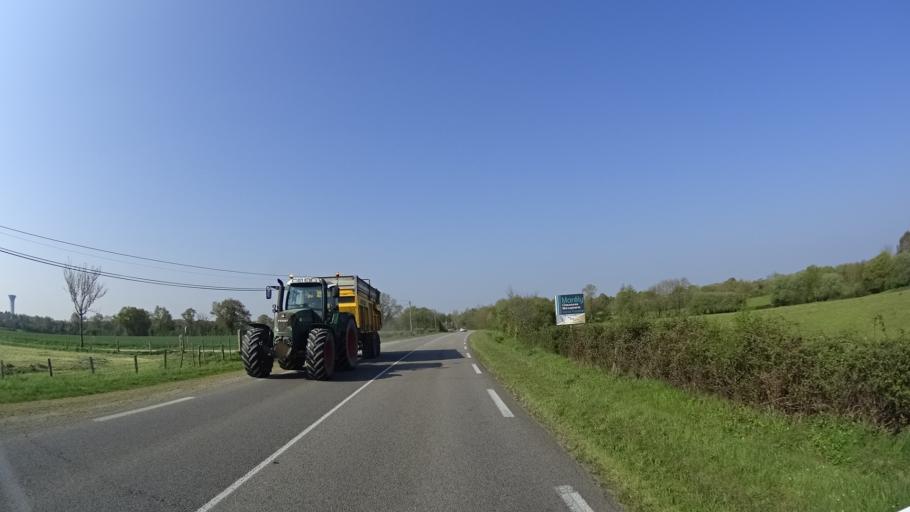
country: FR
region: Pays de la Loire
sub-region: Departement de la Loire-Atlantique
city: Sainte-Pazanne
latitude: 47.1108
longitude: -1.7820
